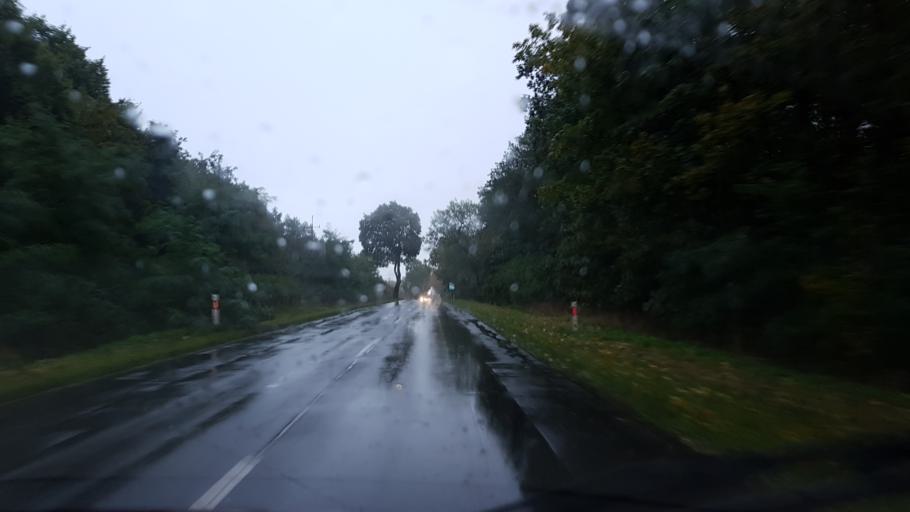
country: PL
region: Greater Poland Voivodeship
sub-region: Powiat pilski
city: Szydlowo
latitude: 53.1563
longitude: 16.6739
